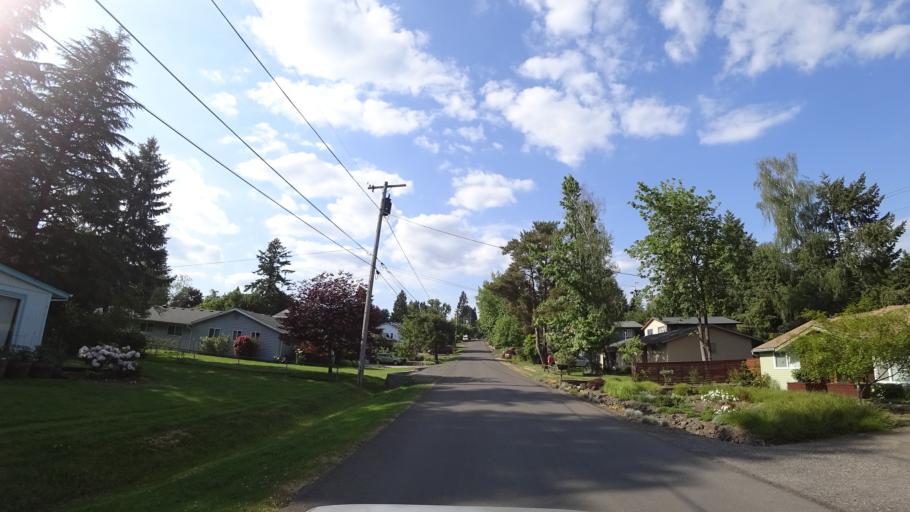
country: US
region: Oregon
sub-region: Washington County
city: Garden Home-Whitford
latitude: 45.4632
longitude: -122.7443
